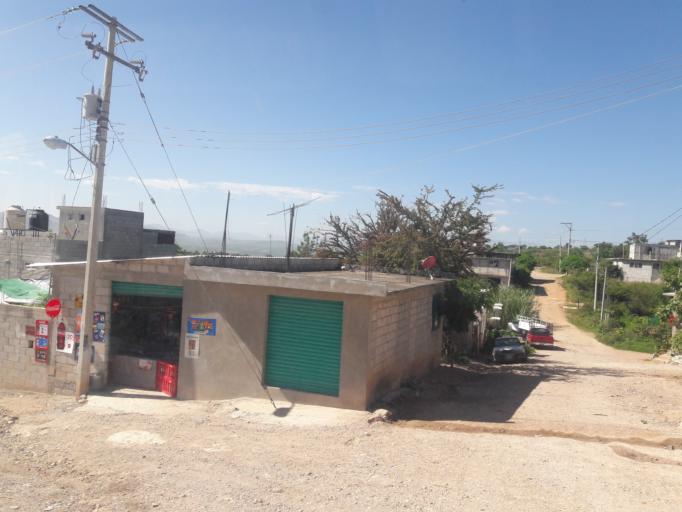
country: MX
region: Oaxaca
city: Ciudad de Huajuapam de Leon
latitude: 17.8038
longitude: -97.8047
